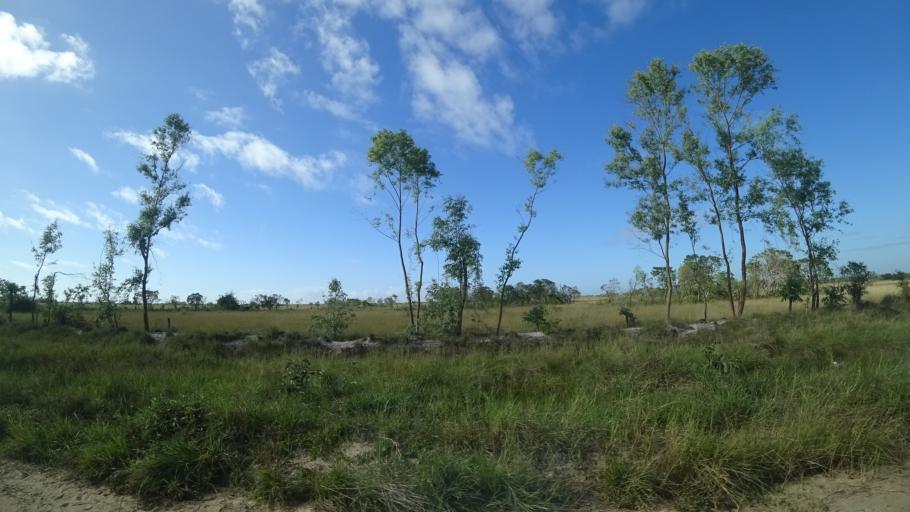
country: MZ
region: Sofala
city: Beira
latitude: -19.7212
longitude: 34.9988
